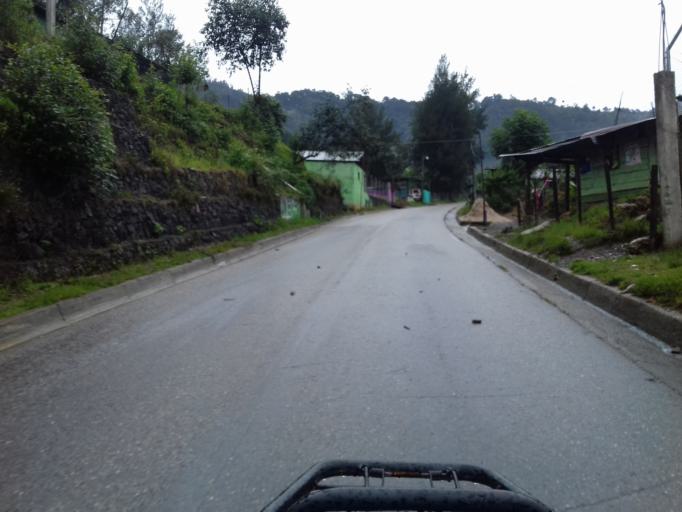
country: GT
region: Quiche
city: Nebaj
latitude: 15.3850
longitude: -91.1118
